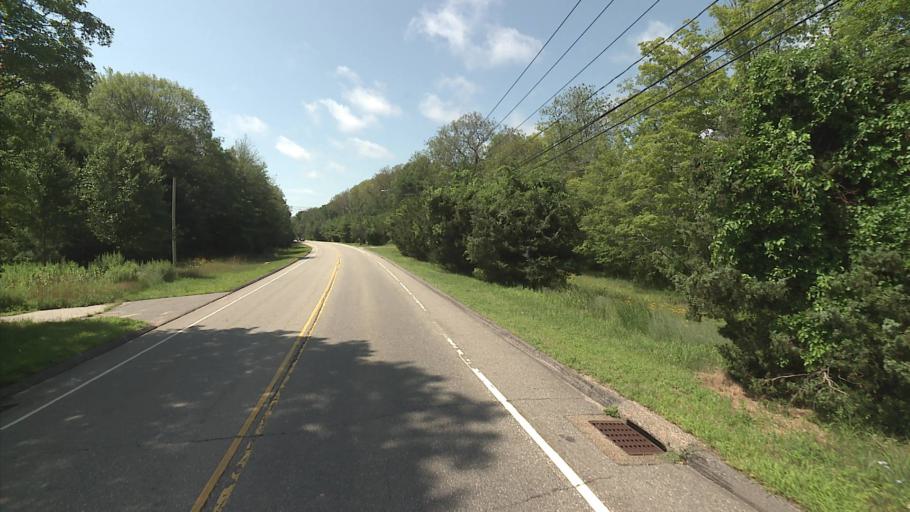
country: US
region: Connecticut
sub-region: Middlesex County
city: Westbrook Center
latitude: 41.3178
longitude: -72.4329
